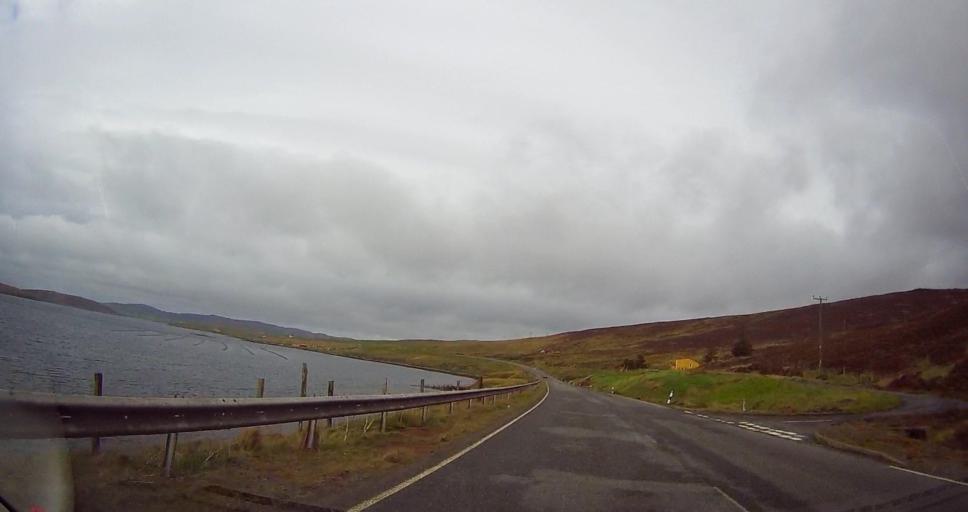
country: GB
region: Scotland
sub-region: Shetland Islands
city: Lerwick
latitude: 60.3682
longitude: -1.2952
